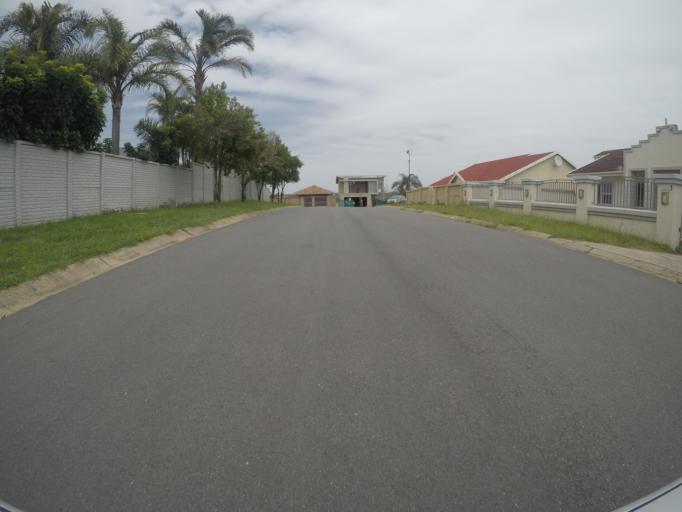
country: ZA
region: Eastern Cape
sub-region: Buffalo City Metropolitan Municipality
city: East London
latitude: -32.9645
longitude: 27.9255
